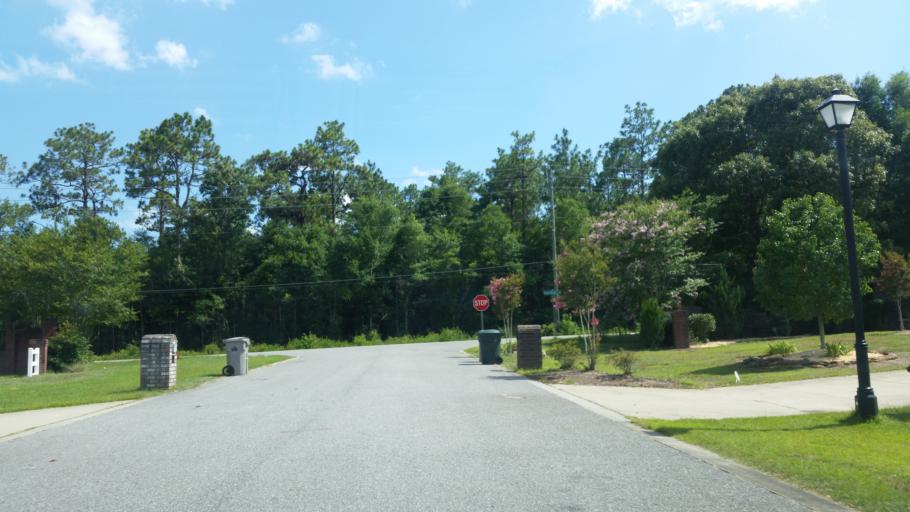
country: US
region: Florida
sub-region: Escambia County
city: Cantonment
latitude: 30.5508
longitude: -87.3833
